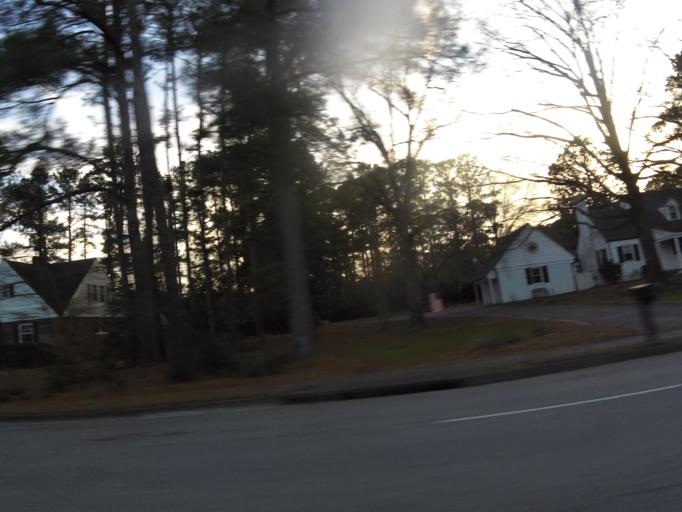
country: US
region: Virginia
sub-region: City of Franklin
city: Franklin
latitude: 36.6833
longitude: -76.9402
